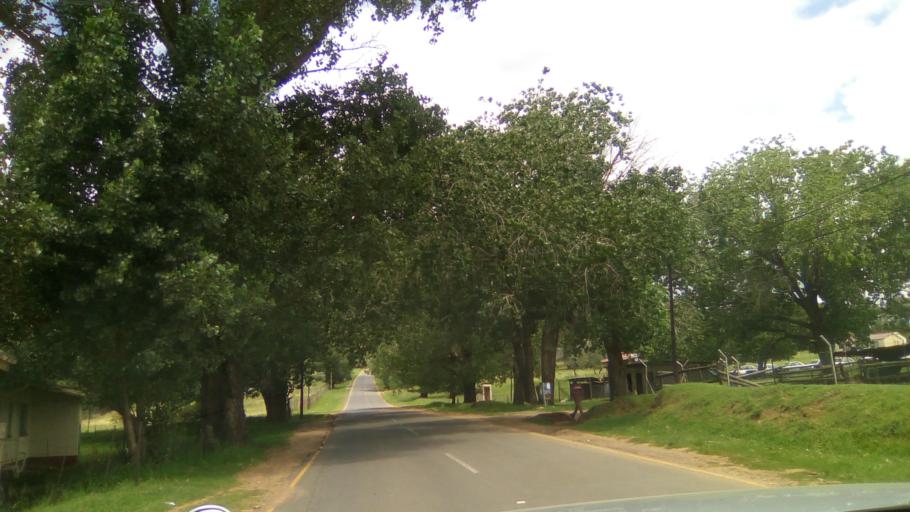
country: LS
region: Maseru
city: Nako
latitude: -29.6269
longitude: 27.5030
